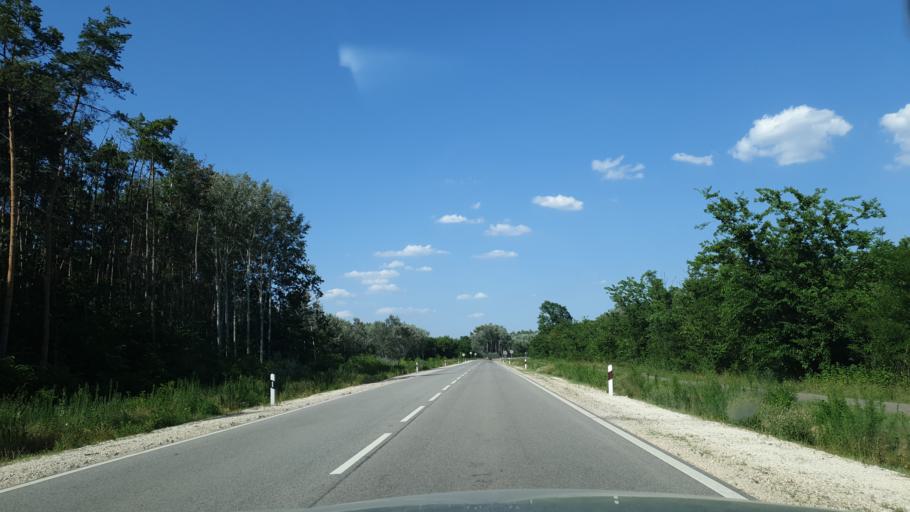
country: HU
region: Csongrad
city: Asotthalom
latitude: 46.2173
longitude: 19.8041
